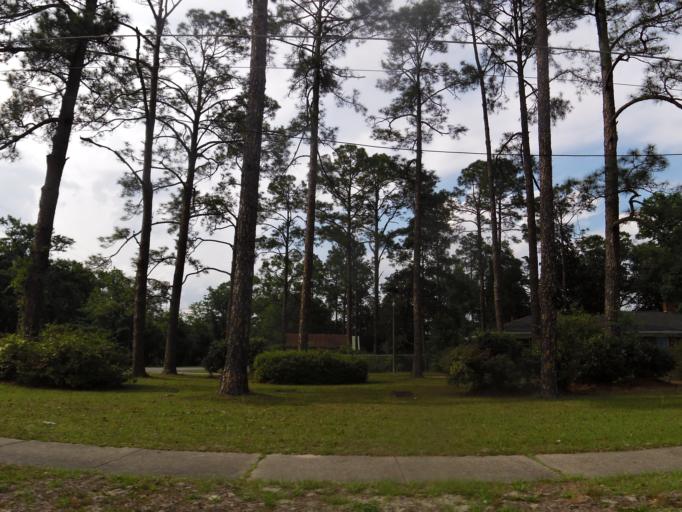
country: US
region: Georgia
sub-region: Charlton County
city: Folkston
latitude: 30.8323
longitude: -82.0006
